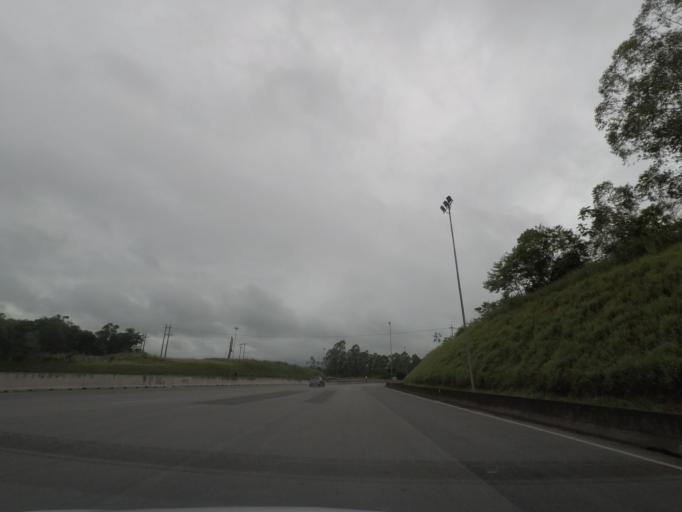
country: BR
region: Sao Paulo
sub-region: Cajati
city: Cajati
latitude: -24.7221
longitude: -48.0811
